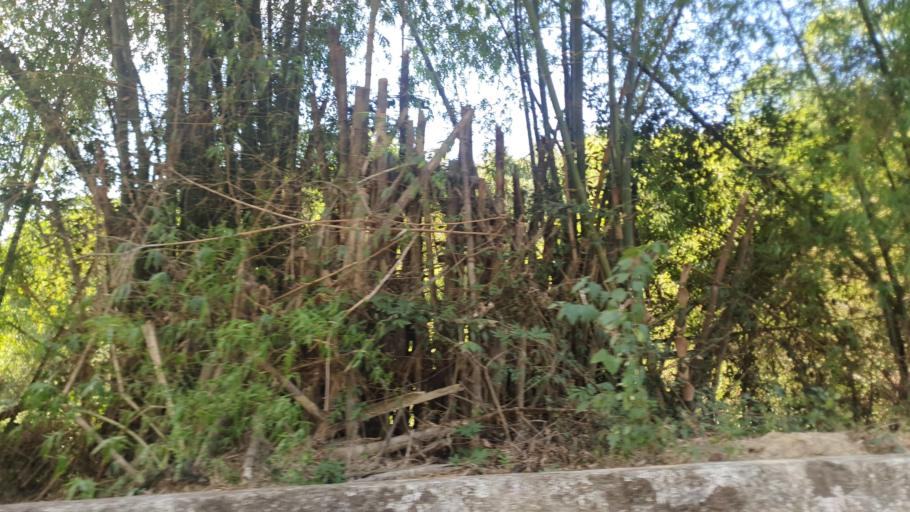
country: TW
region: Taiwan
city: Yujing
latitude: 23.0441
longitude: 120.3974
